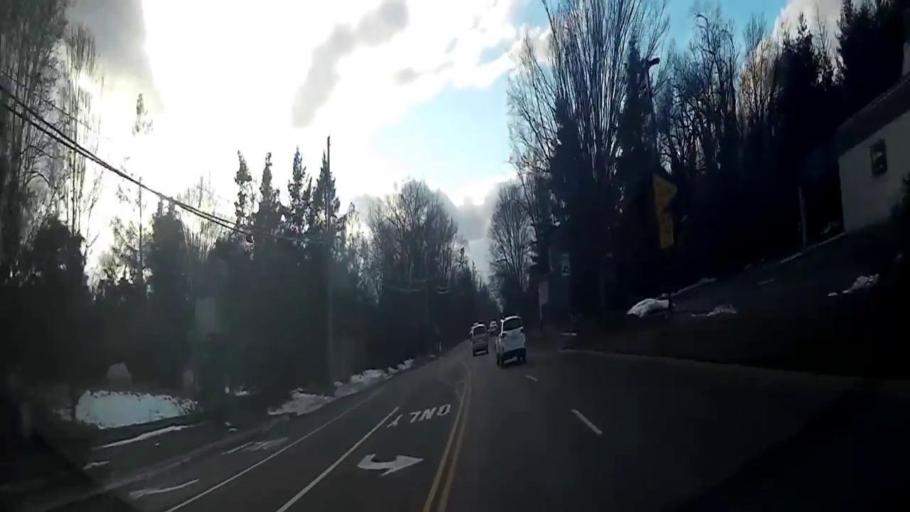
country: US
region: New Jersey
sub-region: Burlington County
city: Marlton
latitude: 39.8562
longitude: -74.9224
